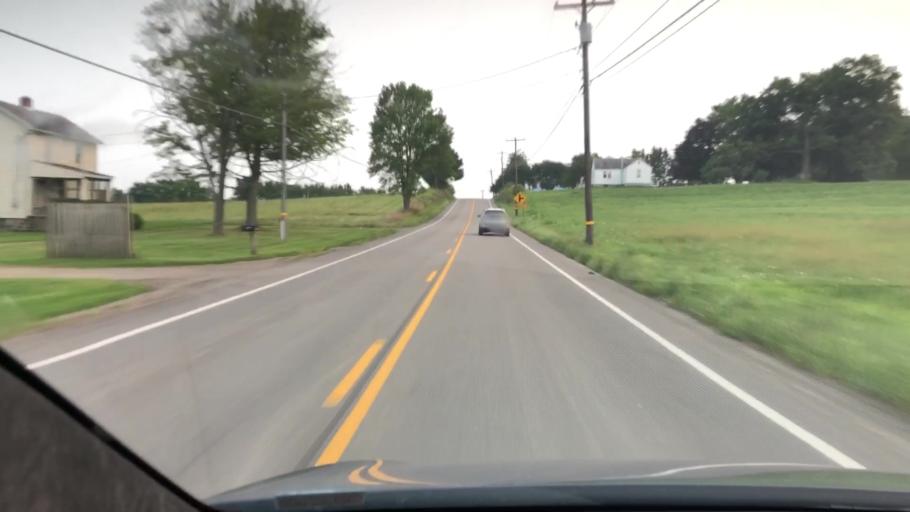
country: US
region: Pennsylvania
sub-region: Mercer County
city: Grove City
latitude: 41.1484
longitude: -80.0068
